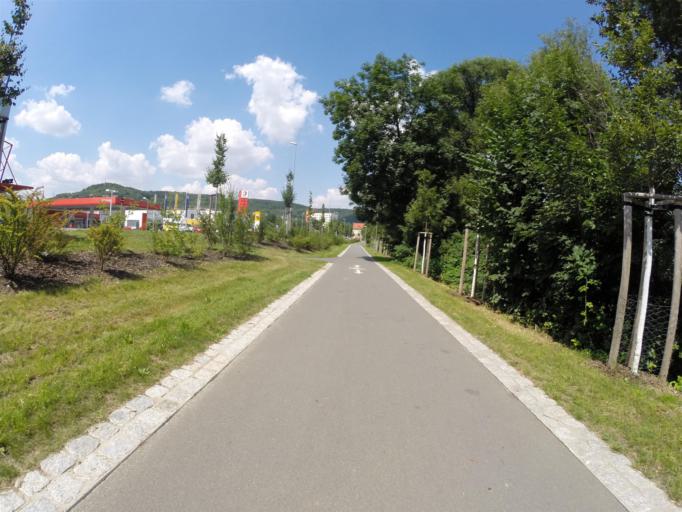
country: DE
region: Thuringia
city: Jena
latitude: 50.9327
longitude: 11.5945
